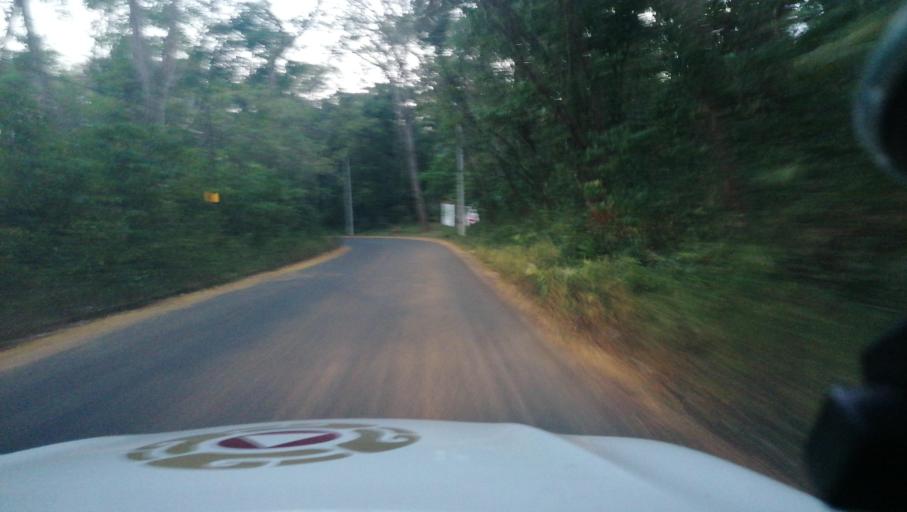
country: MX
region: Chiapas
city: Veinte de Noviembre
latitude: 15.0139
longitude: -92.2462
